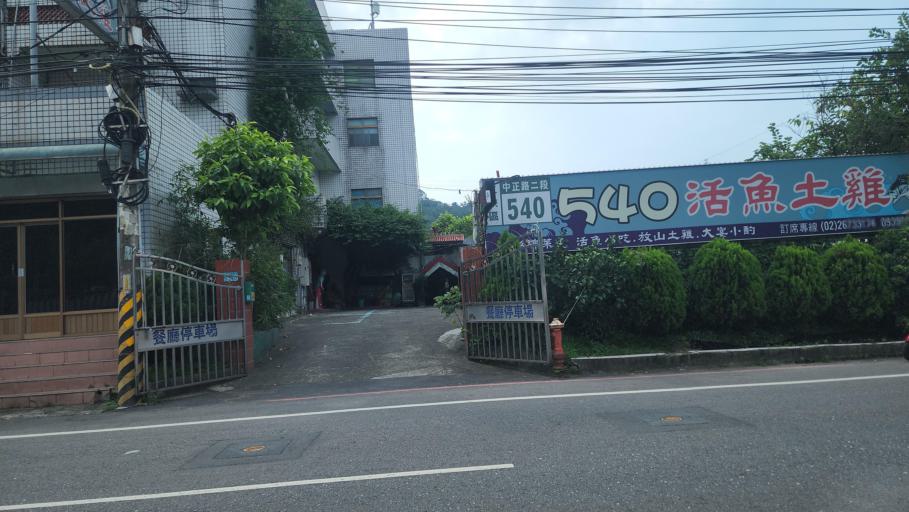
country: TW
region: Taiwan
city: Daxi
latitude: 24.9063
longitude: 121.3603
